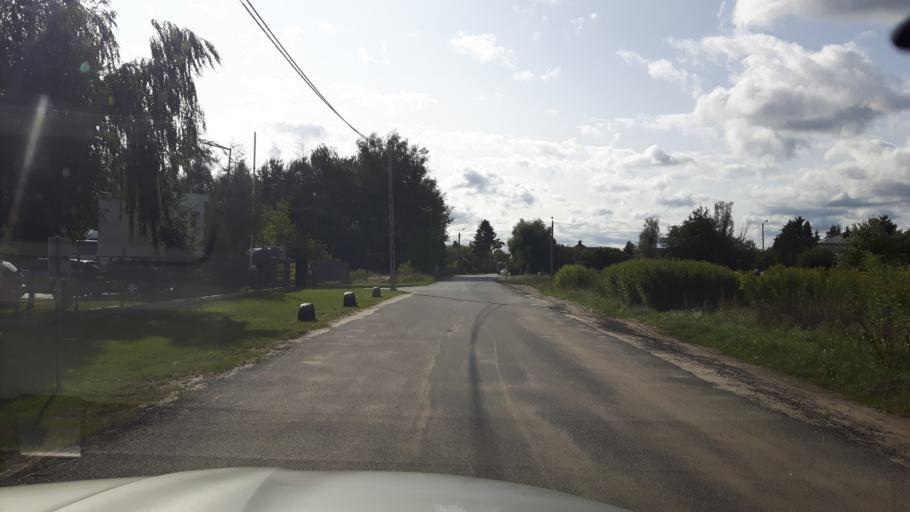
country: PL
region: Masovian Voivodeship
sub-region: Powiat wolominski
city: Marki
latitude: 52.3339
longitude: 21.0908
